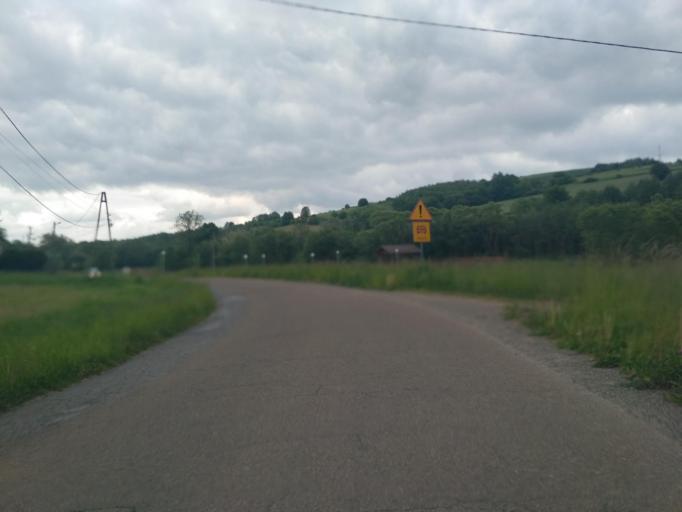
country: PL
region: Subcarpathian Voivodeship
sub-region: Powiat jasielski
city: Tarnowiec
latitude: 49.6803
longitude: 21.5946
